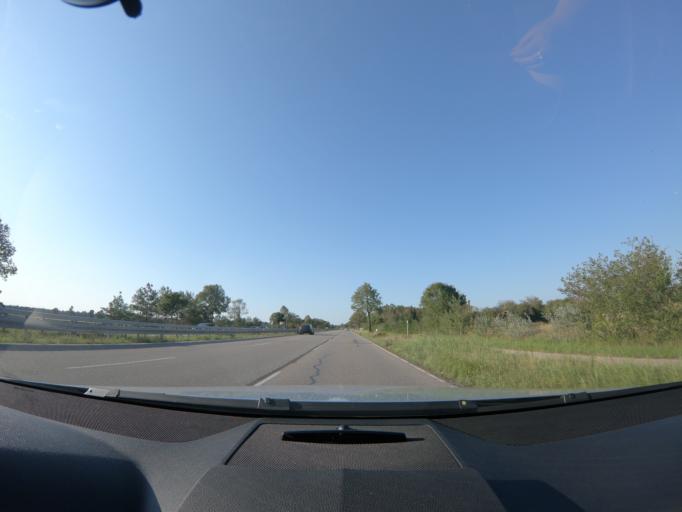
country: DE
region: Bavaria
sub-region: Upper Bavaria
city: Oberschleissheim
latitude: 48.2159
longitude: 11.5879
